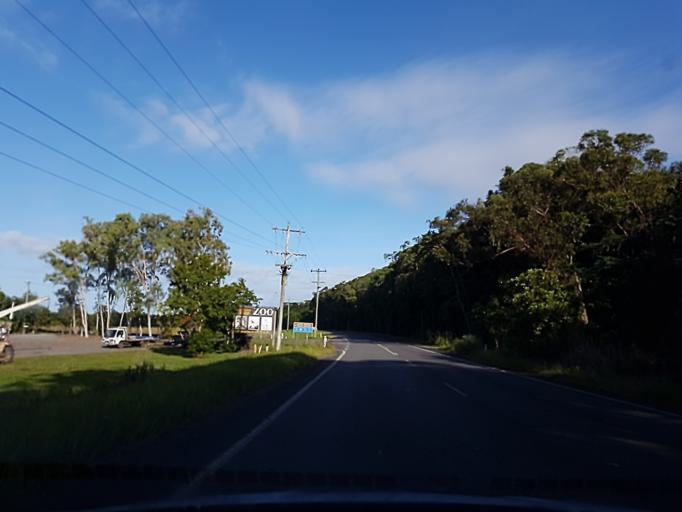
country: AU
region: Queensland
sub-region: Cairns
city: Port Douglas
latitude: -16.3174
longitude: 145.4038
